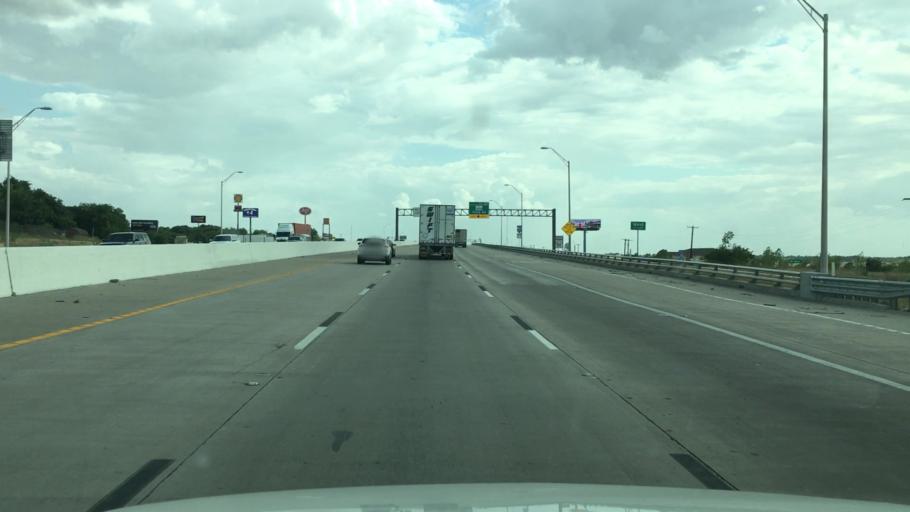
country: US
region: Texas
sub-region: McLennan County
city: West
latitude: 31.8070
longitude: -97.0996
